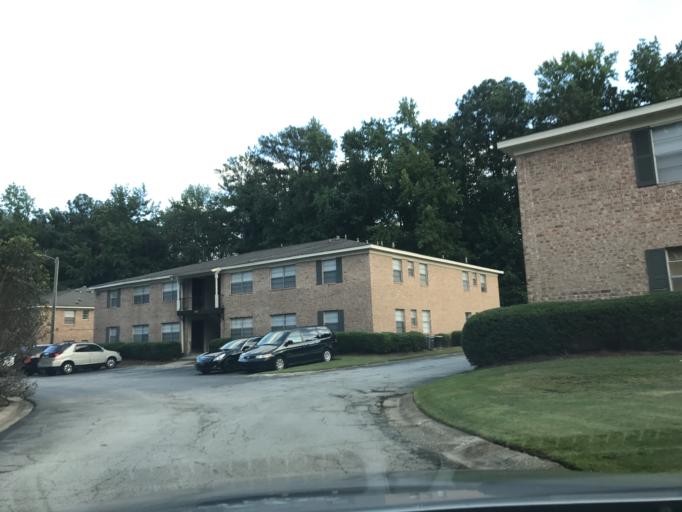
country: US
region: Georgia
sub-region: Douglas County
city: Douglasville
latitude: 33.7478
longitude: -84.7294
